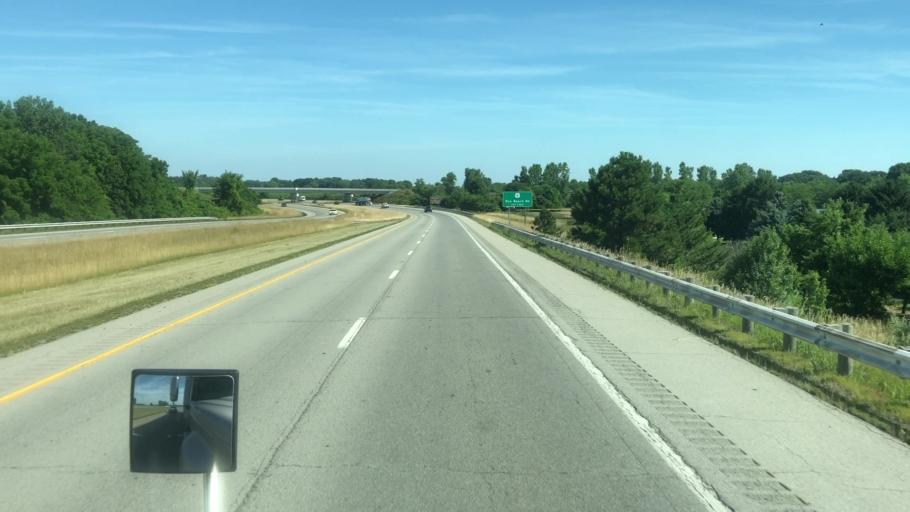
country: US
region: Ohio
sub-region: Erie County
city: Huron
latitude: 41.3940
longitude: -82.5740
